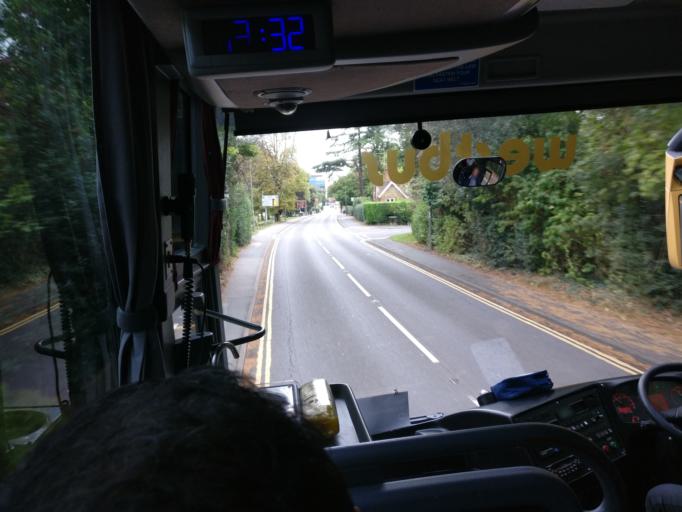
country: GB
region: England
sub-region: Surrey
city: Woking
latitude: 51.3247
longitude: -0.5610
